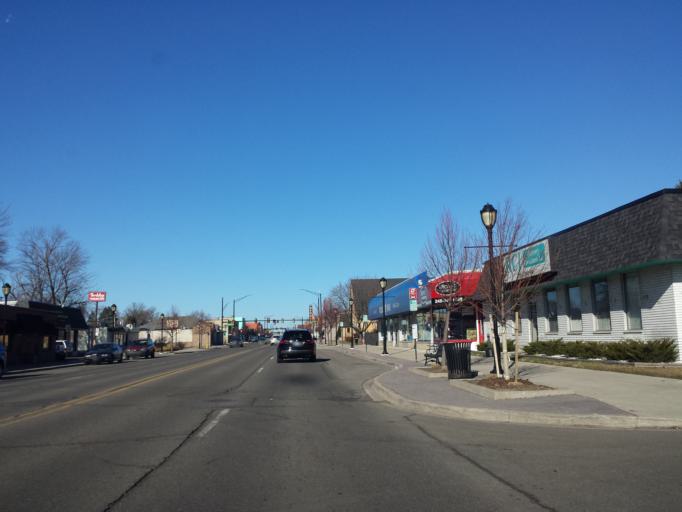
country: US
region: Michigan
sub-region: Oakland County
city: Berkley
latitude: 42.5032
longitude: -83.1861
